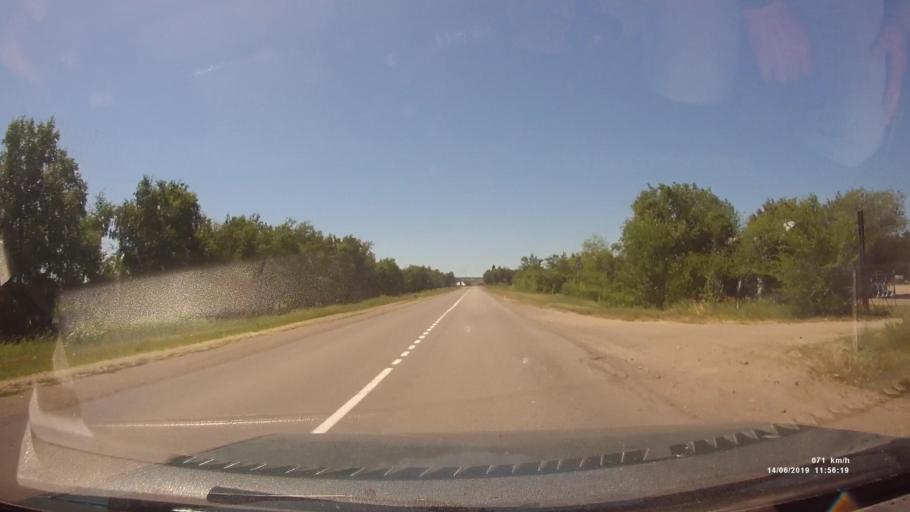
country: RU
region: Rostov
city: Kazanskaya
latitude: 49.8038
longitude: 41.1631
